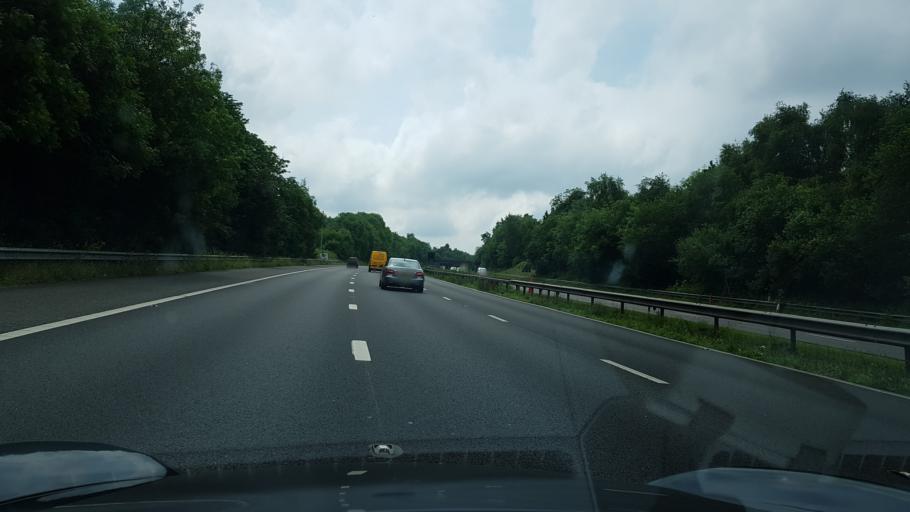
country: GB
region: England
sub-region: West Sussex
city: Maidenbower
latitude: 51.1199
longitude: -0.1387
